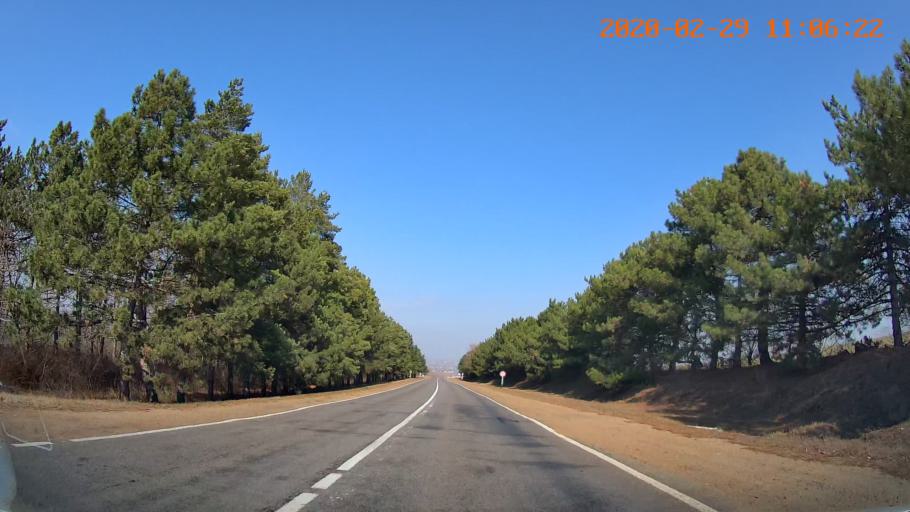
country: MD
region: Criuleni
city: Criuleni
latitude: 47.2137
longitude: 29.1885
